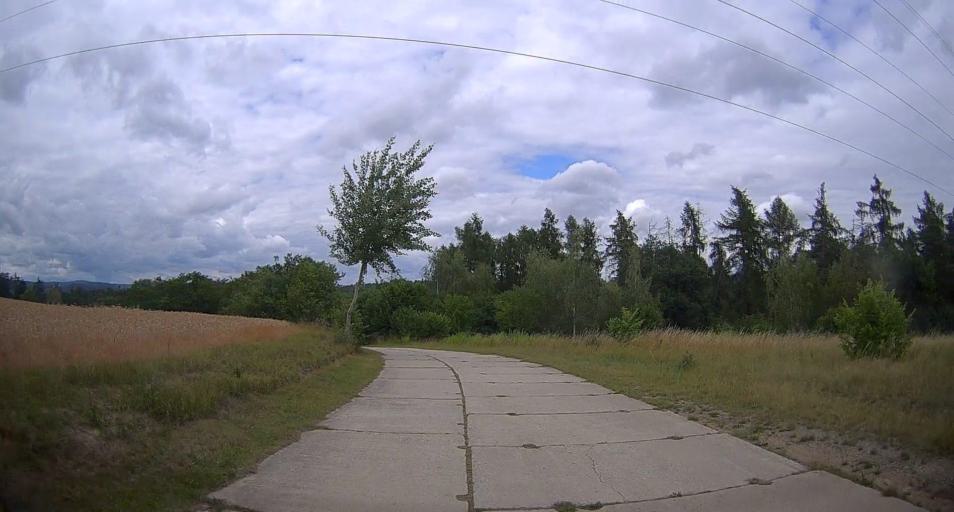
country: CZ
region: South Moravian
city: Lipuvka
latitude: 49.3296
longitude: 16.5376
